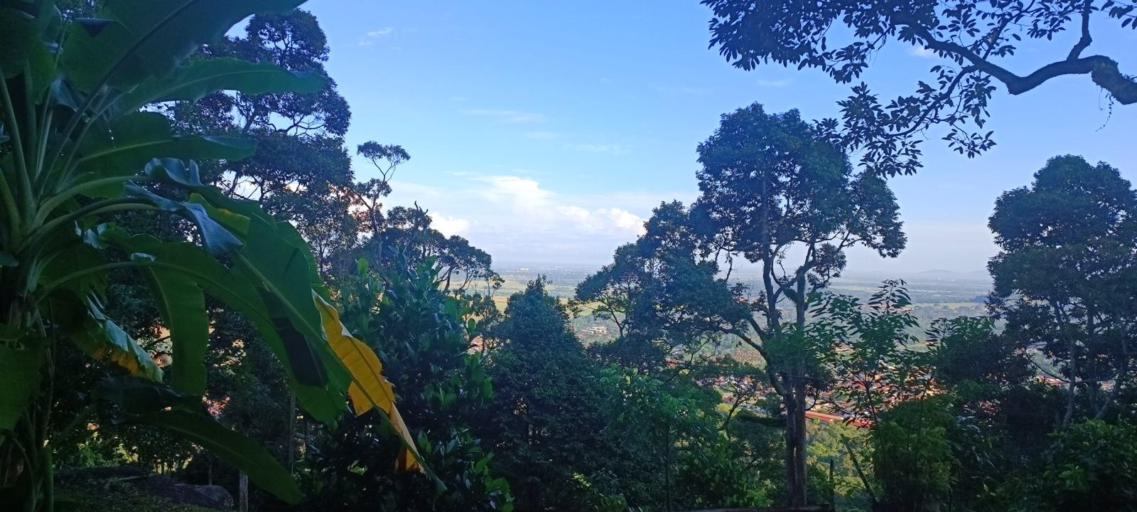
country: MY
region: Penang
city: Bukit Mertajam
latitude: 5.3683
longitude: 100.4762
